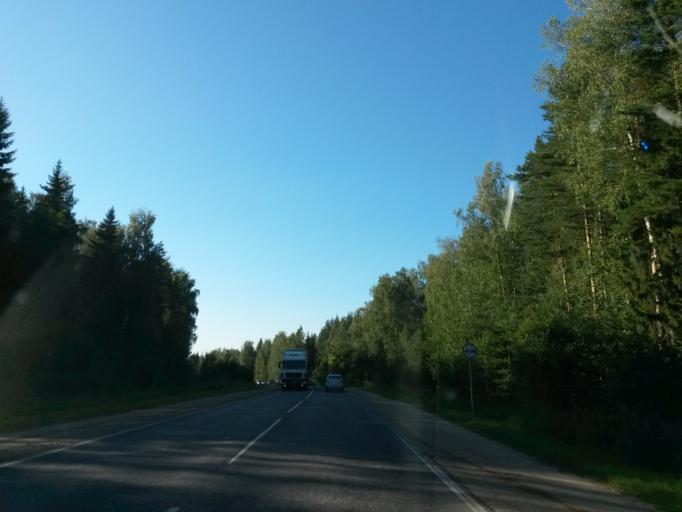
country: RU
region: Ivanovo
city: Novo-Talitsy
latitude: 57.0518
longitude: 40.7352
